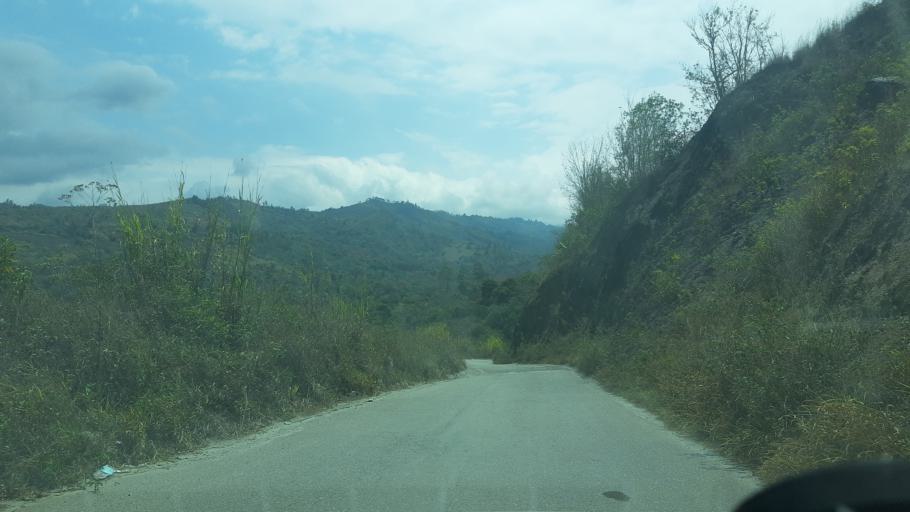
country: CO
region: Boyaca
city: Somondoco
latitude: 5.0128
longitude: -73.3791
